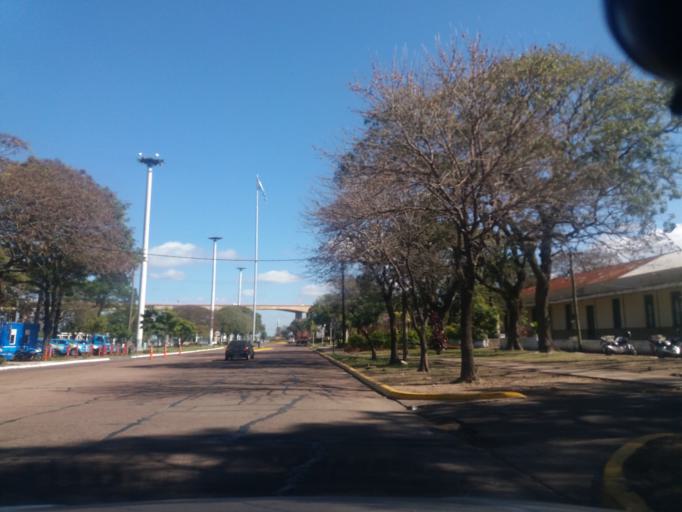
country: AR
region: Corrientes
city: Corrientes
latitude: -27.4736
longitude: -58.8528
